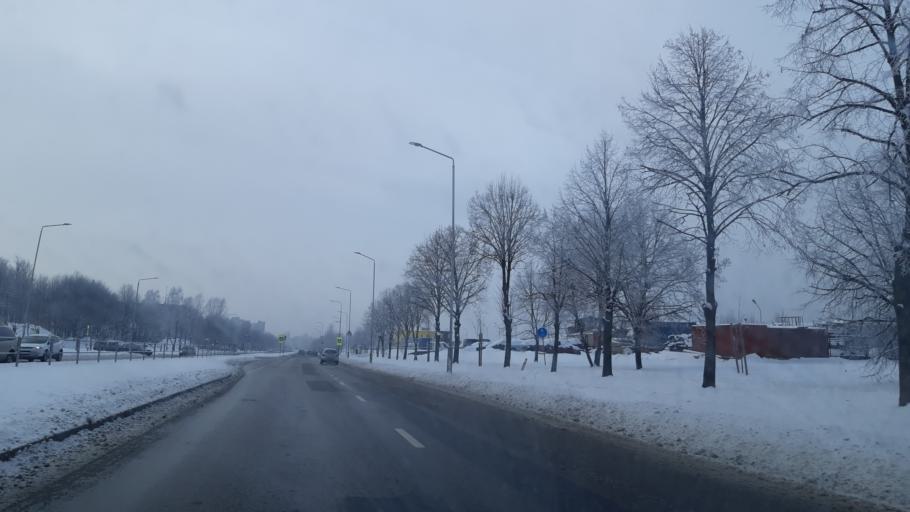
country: LT
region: Kauno apskritis
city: Dainava (Kaunas)
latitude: 54.9311
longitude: 23.9573
